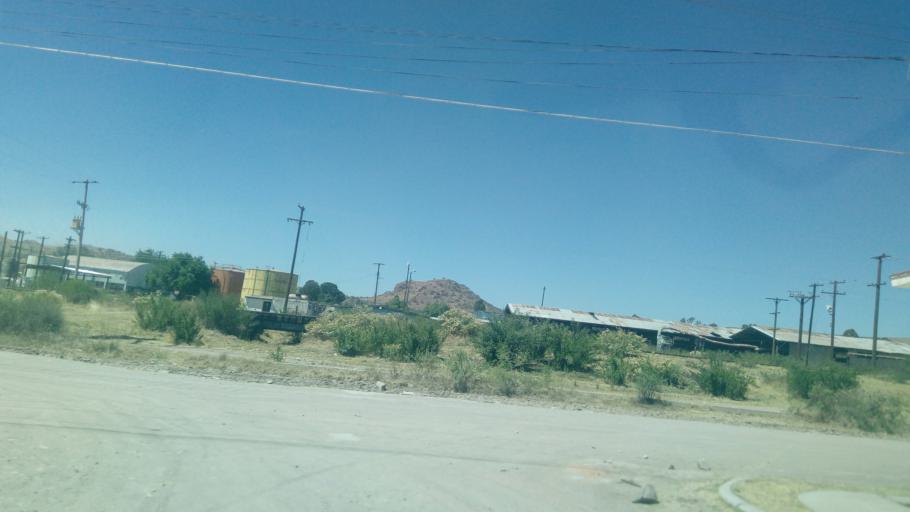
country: MX
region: Durango
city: Victoria de Durango
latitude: 24.0777
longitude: -104.6593
